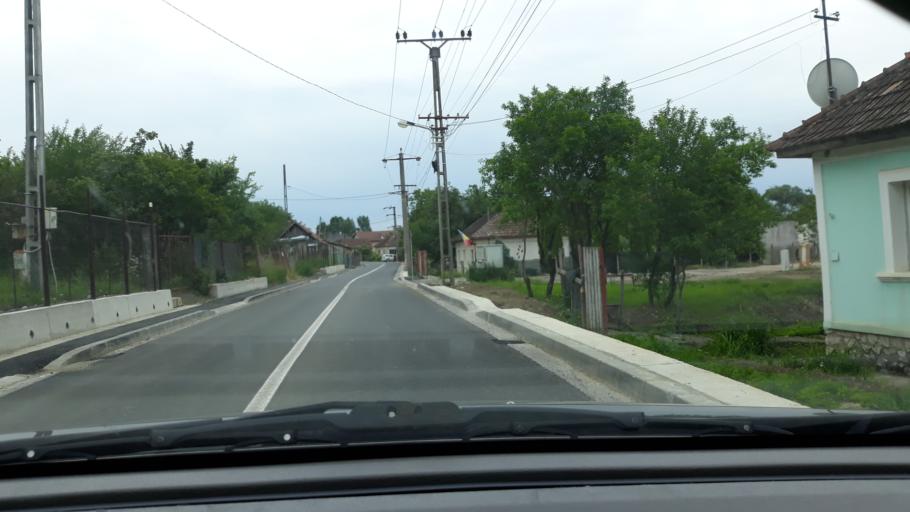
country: RO
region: Bihor
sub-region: Comuna Osorheiu
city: Alparea
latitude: 47.0596
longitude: 22.0073
